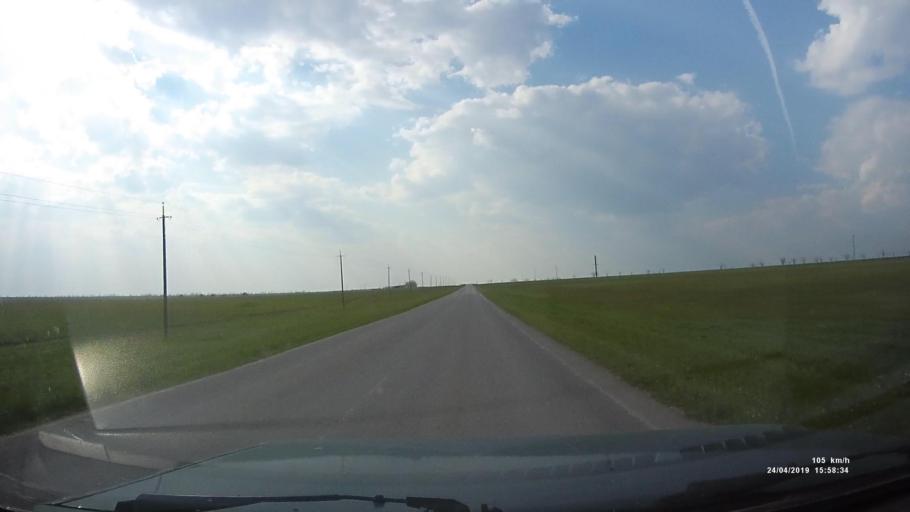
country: RU
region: Kalmykiya
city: Yashalta
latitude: 46.6154
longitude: 42.4878
